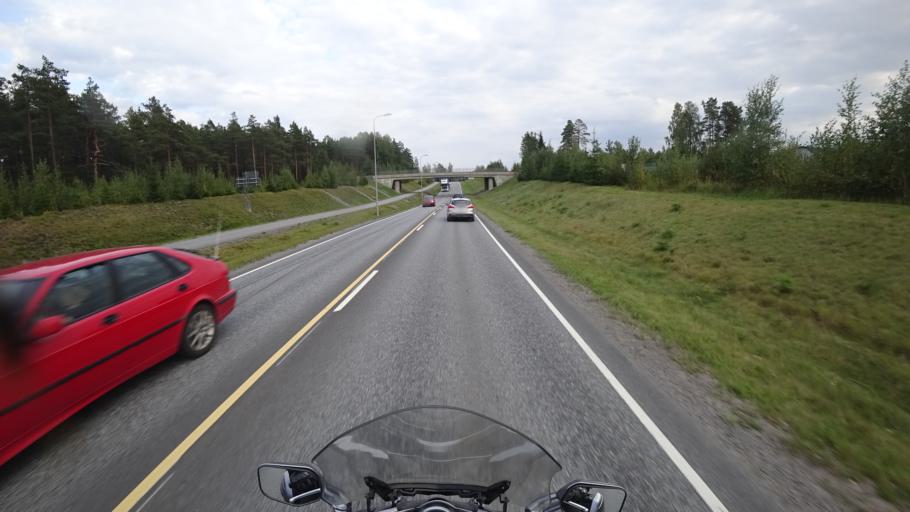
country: FI
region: Uusimaa
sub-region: Raaseporin
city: Karis
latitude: 60.0601
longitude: 23.6393
